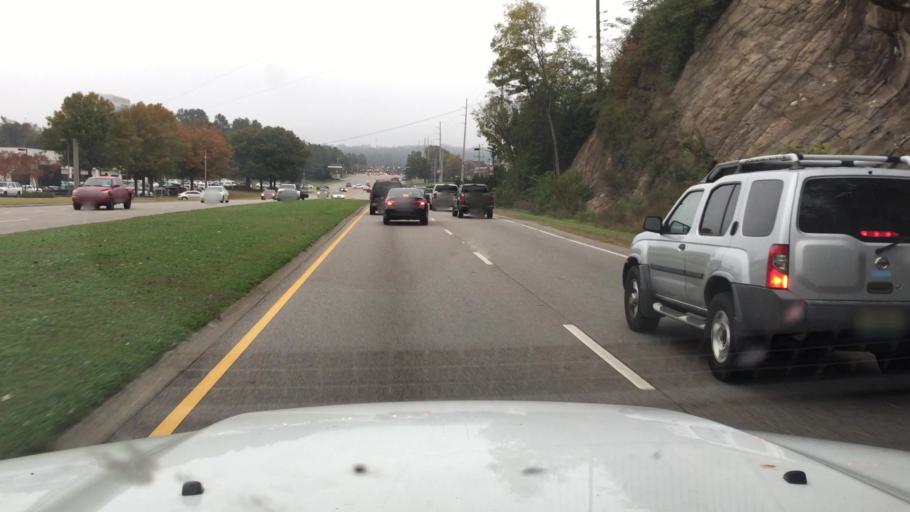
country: US
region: Alabama
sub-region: Jefferson County
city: Hoover
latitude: 33.3742
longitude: -86.8018
